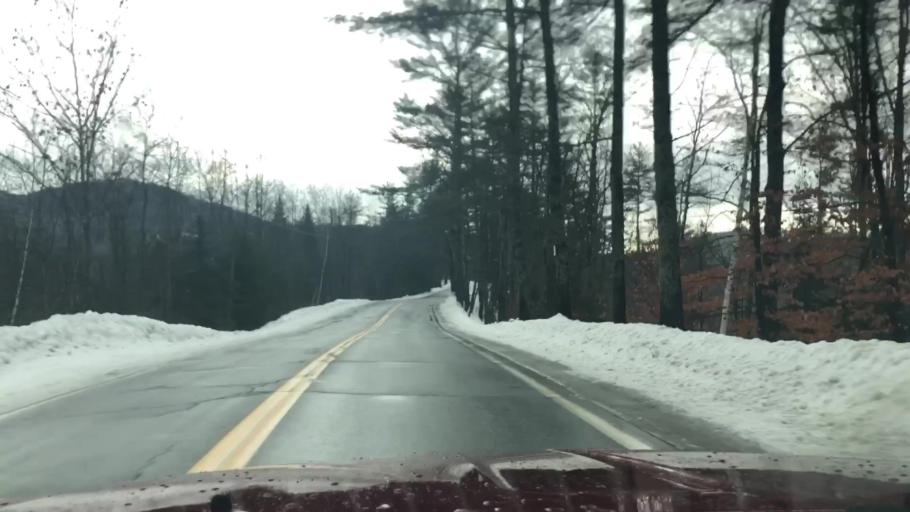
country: US
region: Maine
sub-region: Oxford County
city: West Paris
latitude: 44.4170
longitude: -70.6459
